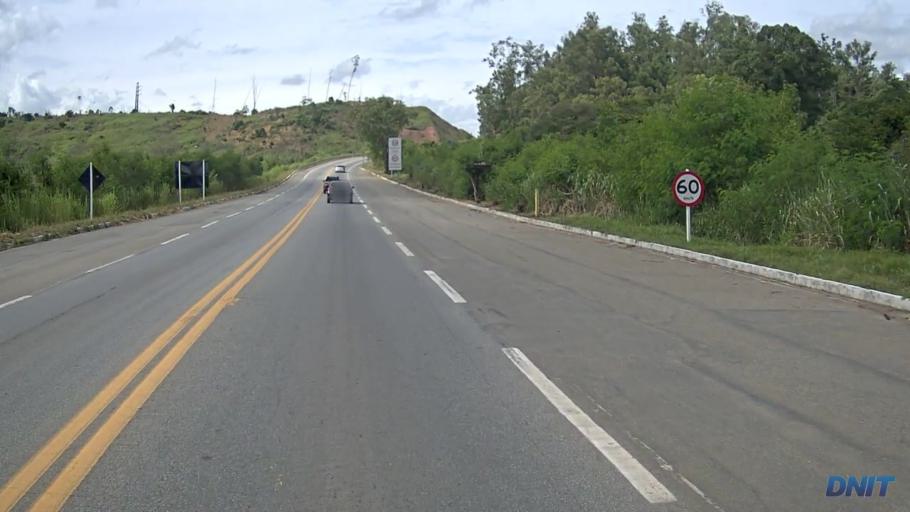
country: BR
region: Minas Gerais
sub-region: Ipatinga
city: Ipatinga
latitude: -19.4382
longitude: -42.5107
